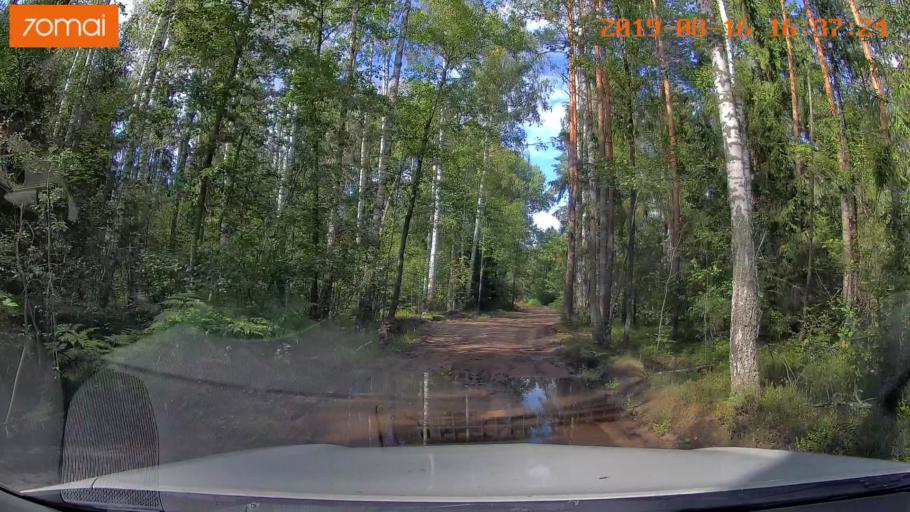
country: BY
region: Mogilev
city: Asipovichy
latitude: 53.2323
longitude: 28.7765
